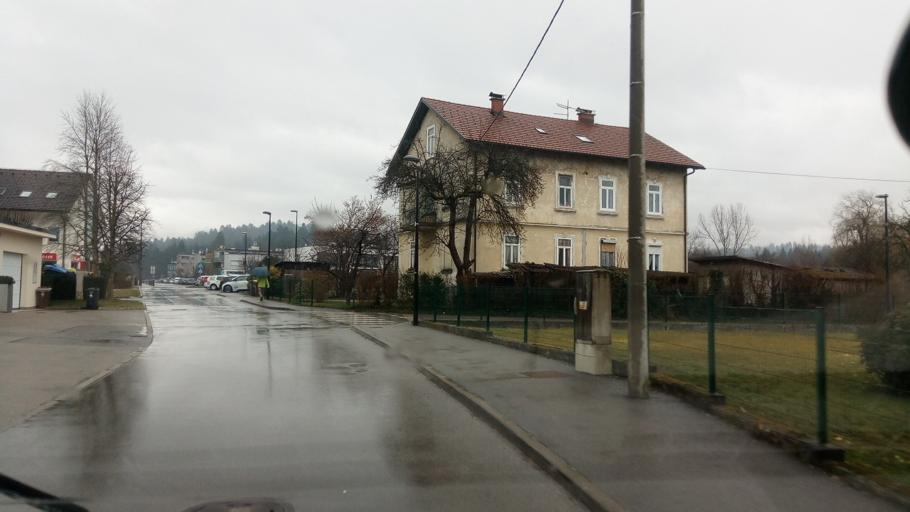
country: SI
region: Ljubljana
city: Ljubljana
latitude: 46.0691
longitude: 14.4697
